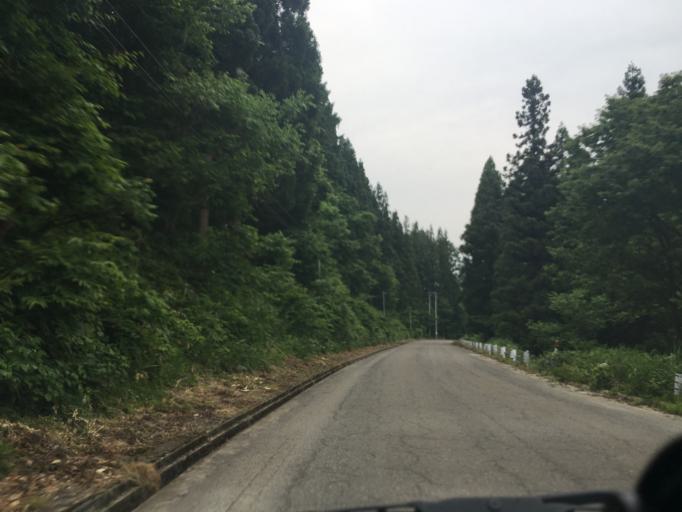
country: JP
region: Fukushima
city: Kitakata
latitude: 37.4874
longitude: 139.7377
